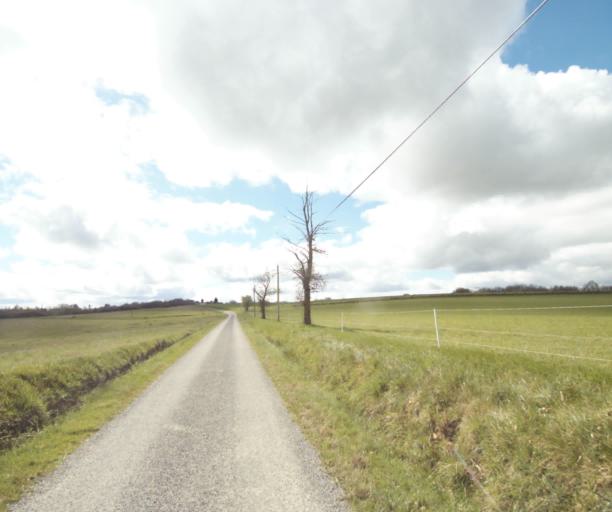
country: FR
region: Midi-Pyrenees
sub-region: Departement de l'Ariege
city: Saverdun
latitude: 43.1847
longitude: 1.5781
